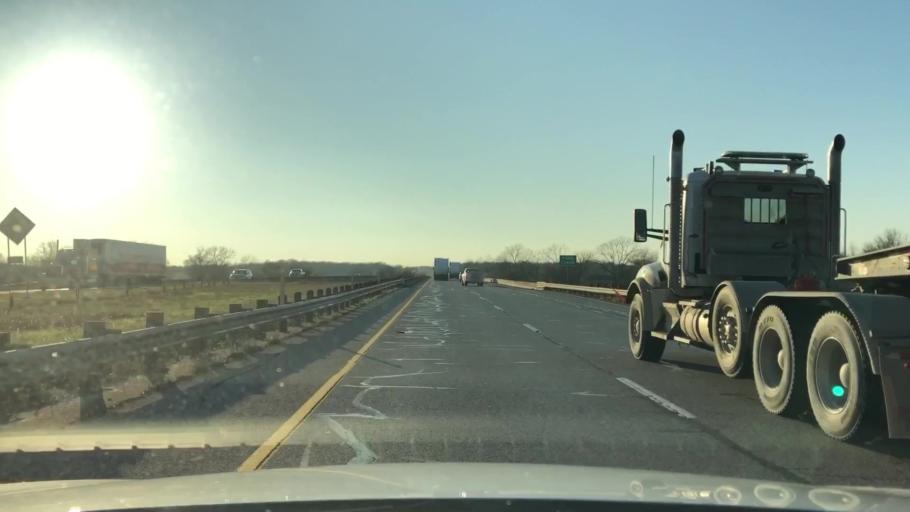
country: US
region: Texas
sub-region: Caldwell County
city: Luling
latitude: 29.6520
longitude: -97.6002
